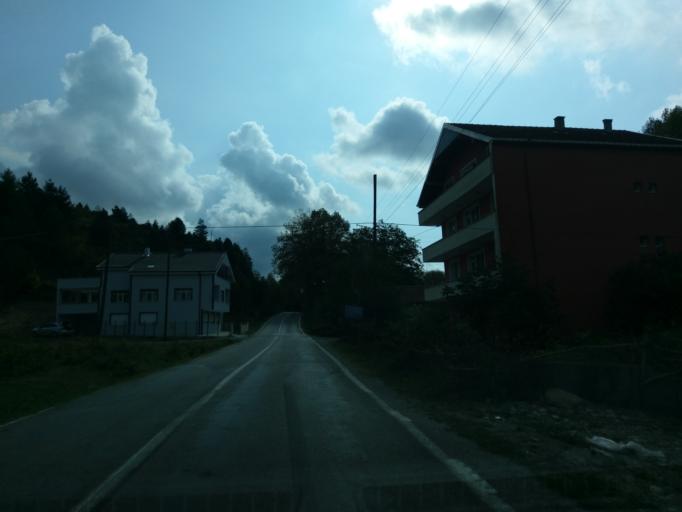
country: TR
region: Sinop
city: Helaldi
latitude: 41.9013
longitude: 34.4567
